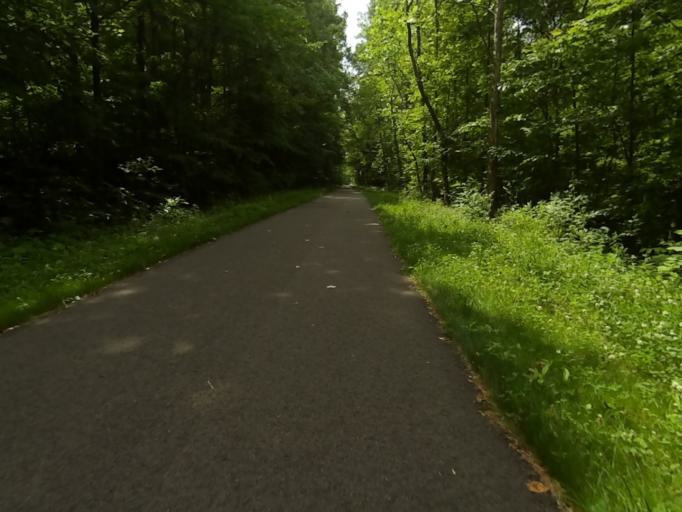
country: US
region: Ohio
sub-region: Summit County
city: Boston Heights
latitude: 41.2714
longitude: -81.5291
